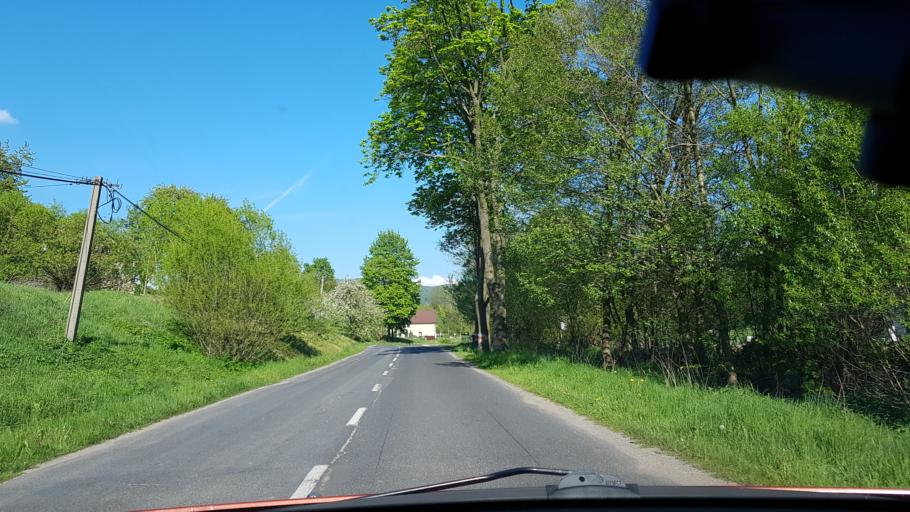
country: PL
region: Lower Silesian Voivodeship
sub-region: Powiat klodzki
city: Nowa Ruda
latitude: 50.5895
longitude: 16.5442
